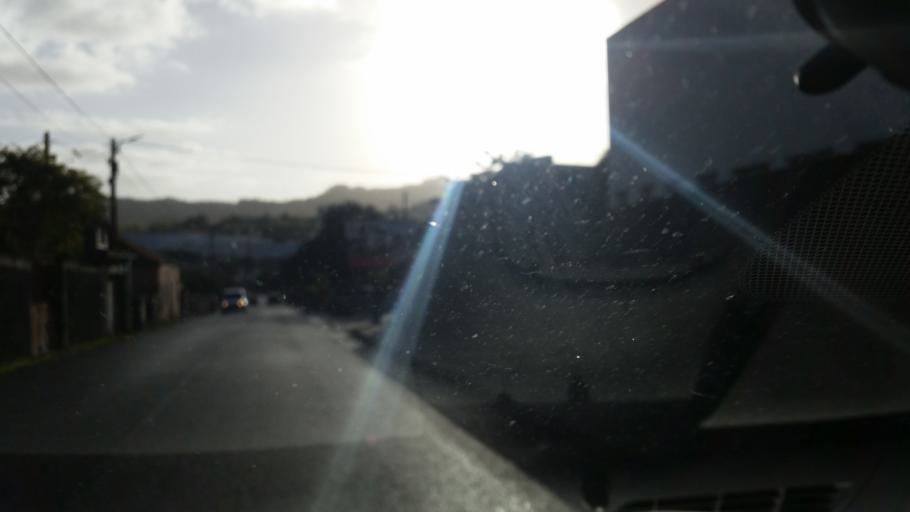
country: PT
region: Porto
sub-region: Santo Tirso
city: Aves
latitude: 41.3553
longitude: -8.4231
